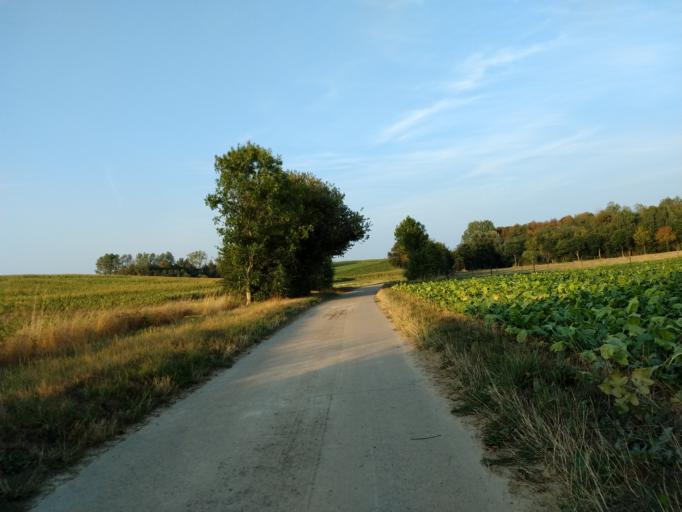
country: BE
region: Flanders
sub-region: Provincie Vlaams-Brabant
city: Hoegaarden
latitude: 50.7858
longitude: 4.8928
